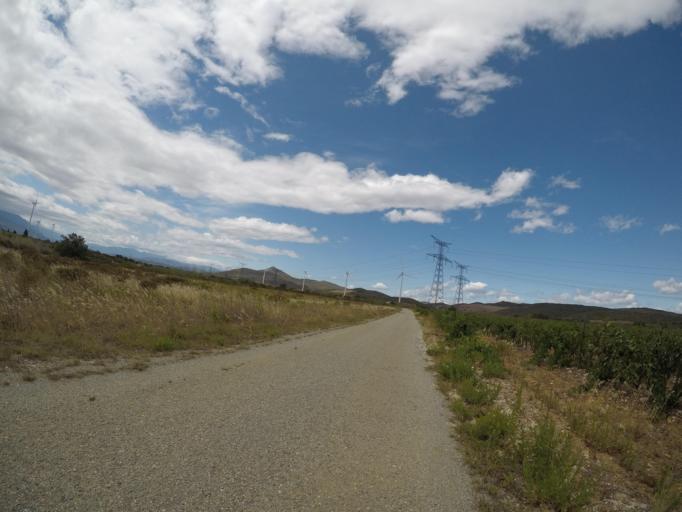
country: FR
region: Languedoc-Roussillon
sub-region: Departement des Pyrenees-Orientales
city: Pezilla-la-Riviere
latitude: 42.7198
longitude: 2.7583
